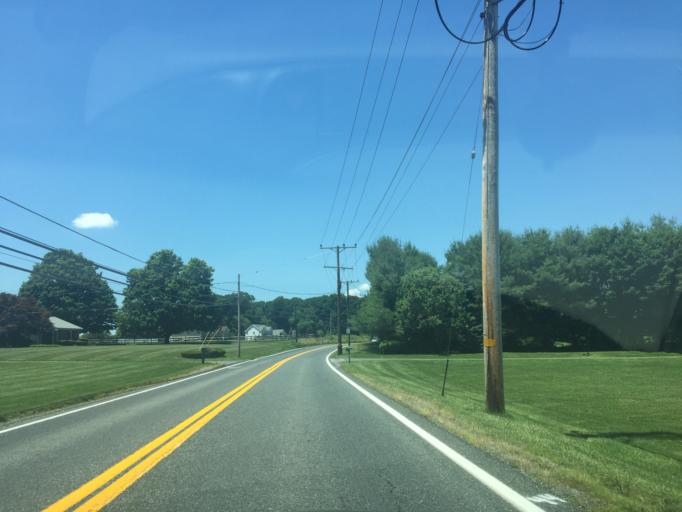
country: US
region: Maryland
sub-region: Harford County
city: Jarrettsville
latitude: 39.6045
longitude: -76.4920
